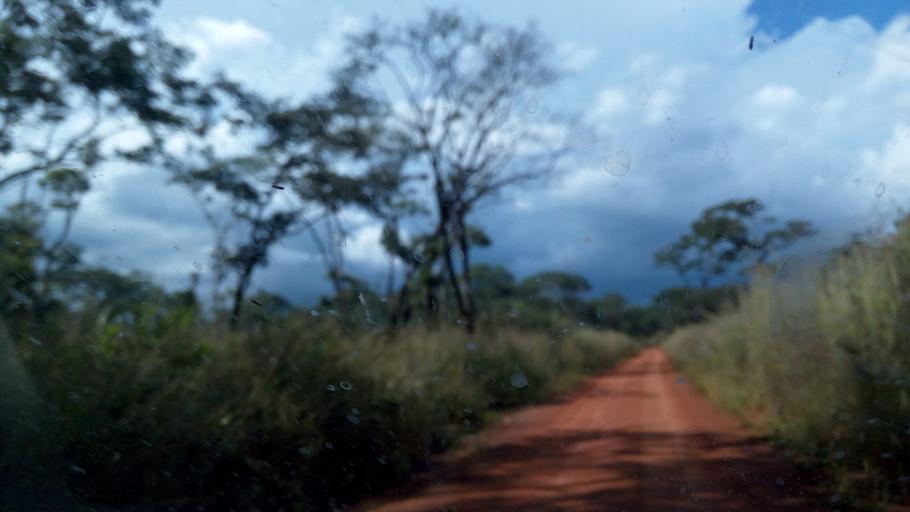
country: ZM
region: Northern
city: Kaputa
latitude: -8.1409
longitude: 29.1116
